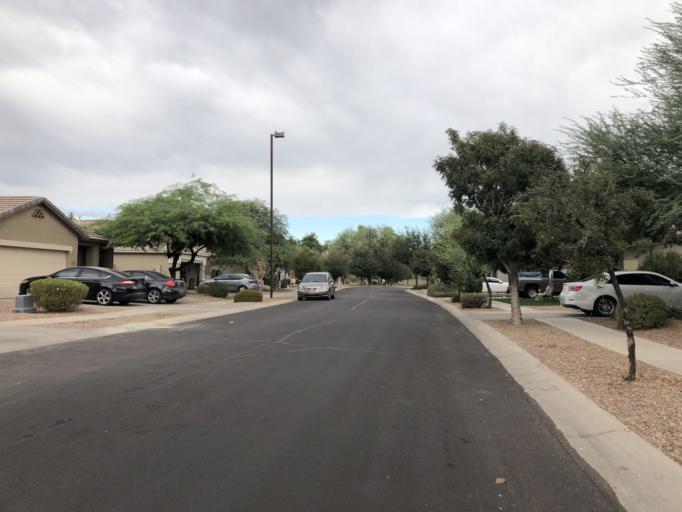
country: US
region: Arizona
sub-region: Maricopa County
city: Queen Creek
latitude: 33.2749
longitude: -111.7014
